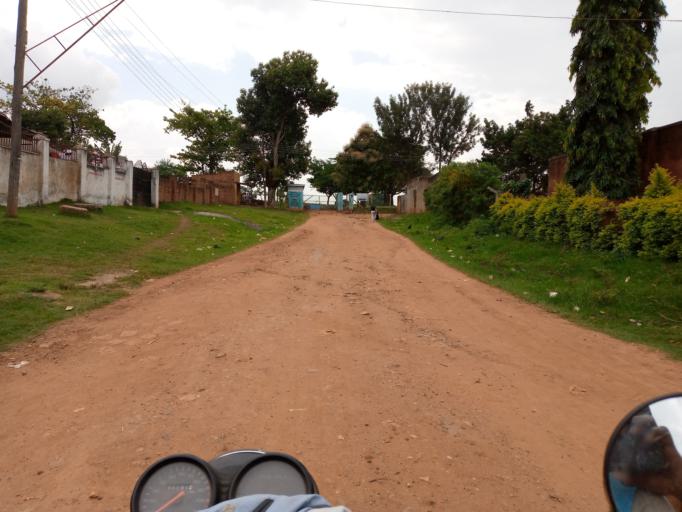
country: UG
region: Eastern Region
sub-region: Mbale District
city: Mbale
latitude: 1.0820
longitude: 34.1702
